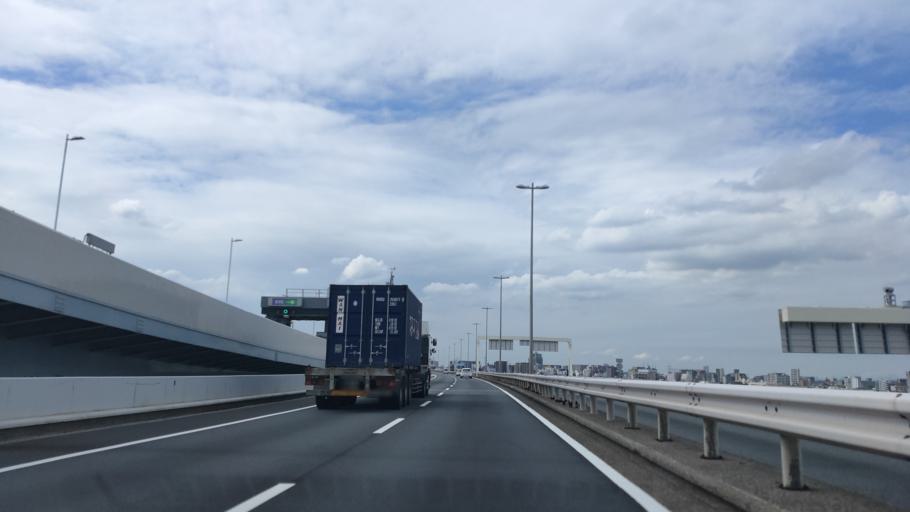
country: JP
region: Tokyo
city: Urayasu
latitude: 35.7003
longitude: 139.8598
